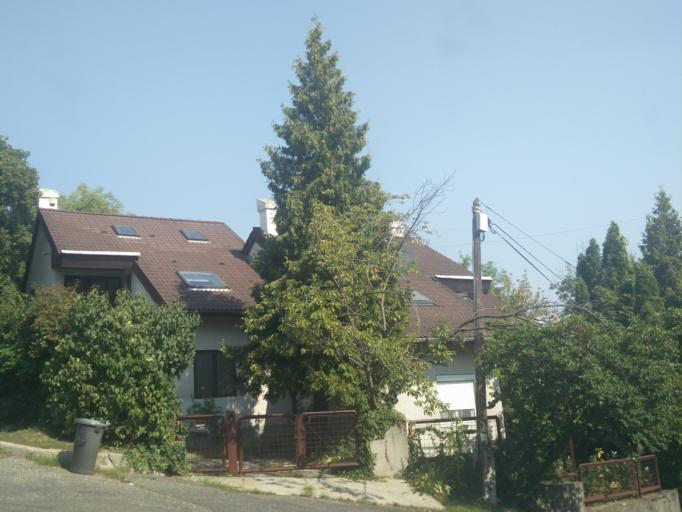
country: HU
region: Budapest
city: Budapest XII. keruelet
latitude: 47.5007
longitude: 18.9995
